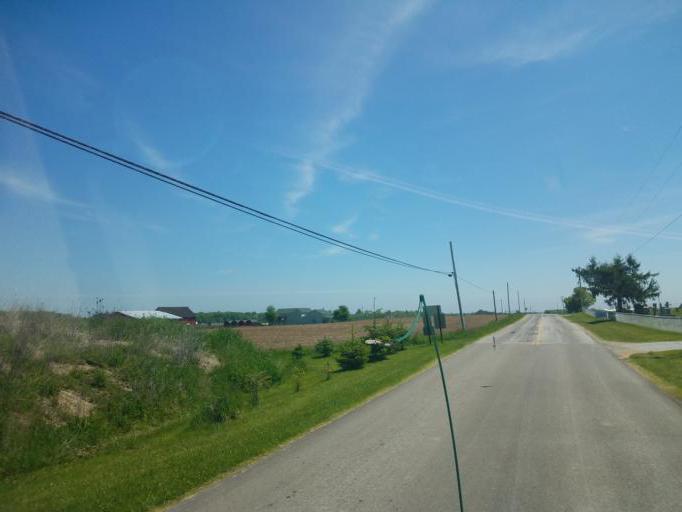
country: US
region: Ohio
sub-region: Wayne County
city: West Salem
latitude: 40.9448
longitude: -82.2052
